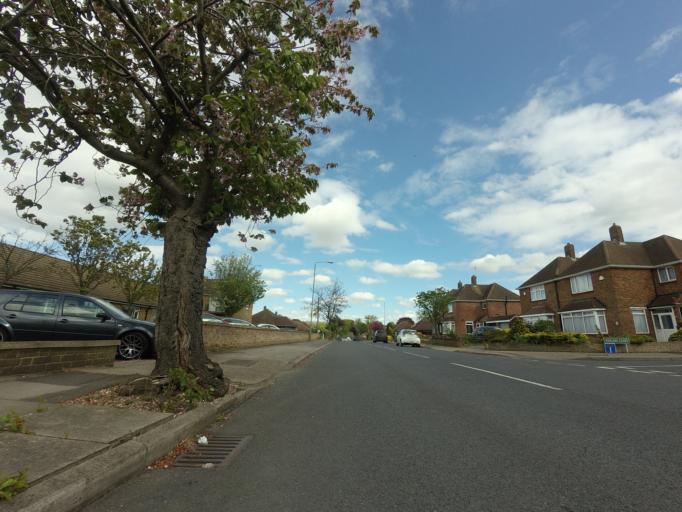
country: GB
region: England
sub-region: Greater London
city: Orpington
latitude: 51.3697
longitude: 0.1200
